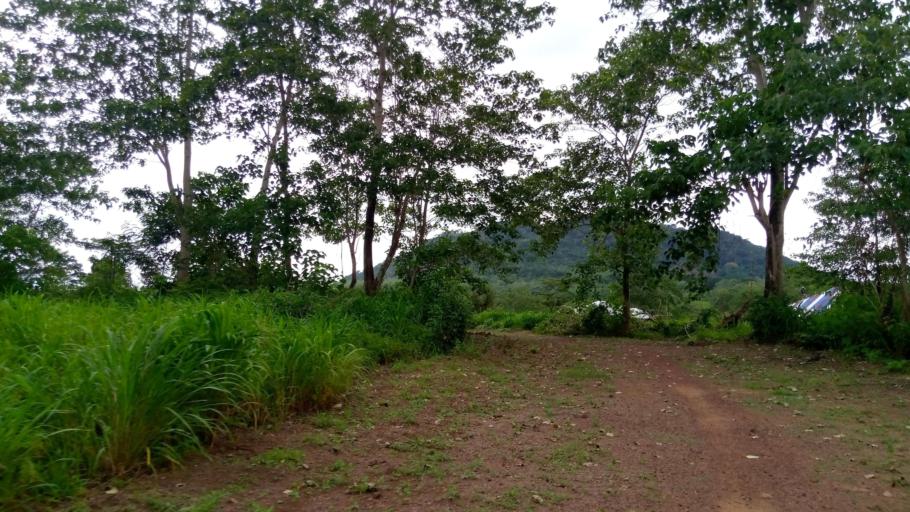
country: SL
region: Southern Province
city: Moyamba
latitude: 8.1604
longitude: -12.4456
